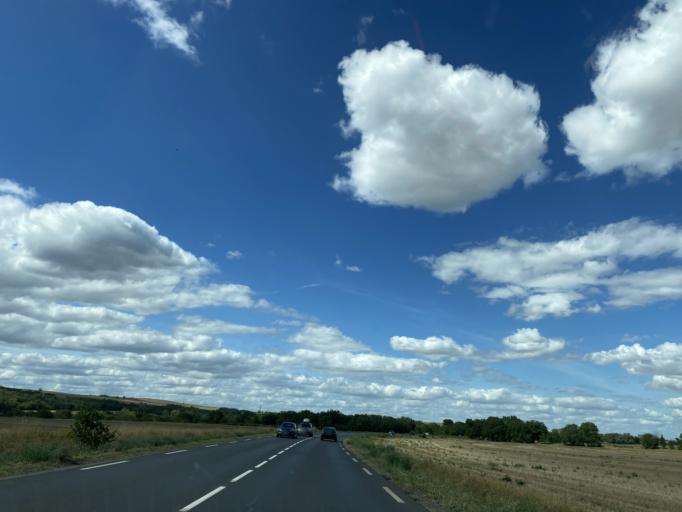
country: FR
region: Auvergne
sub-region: Departement du Puy-de-Dome
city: Mezel
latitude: 45.7562
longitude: 3.2348
